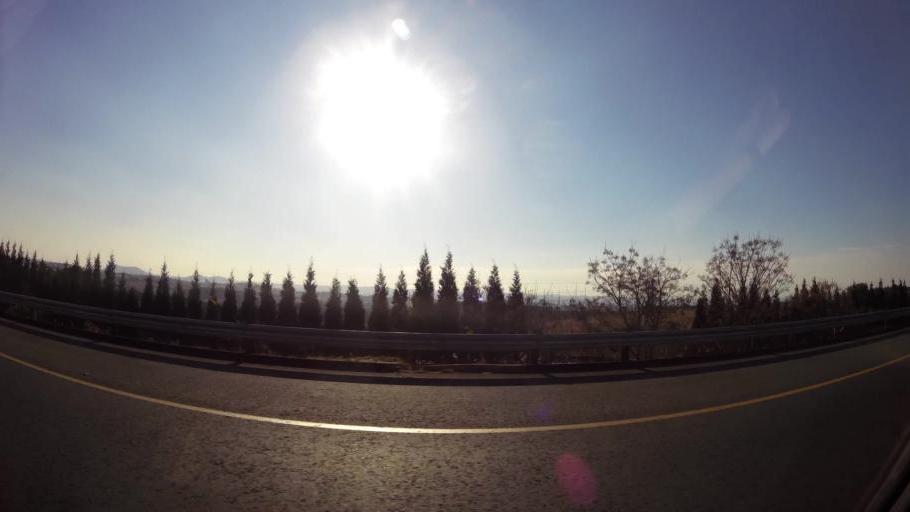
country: ZA
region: Gauteng
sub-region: West Rand District Municipality
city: Muldersdriseloop
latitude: -25.9919
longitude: 27.9134
